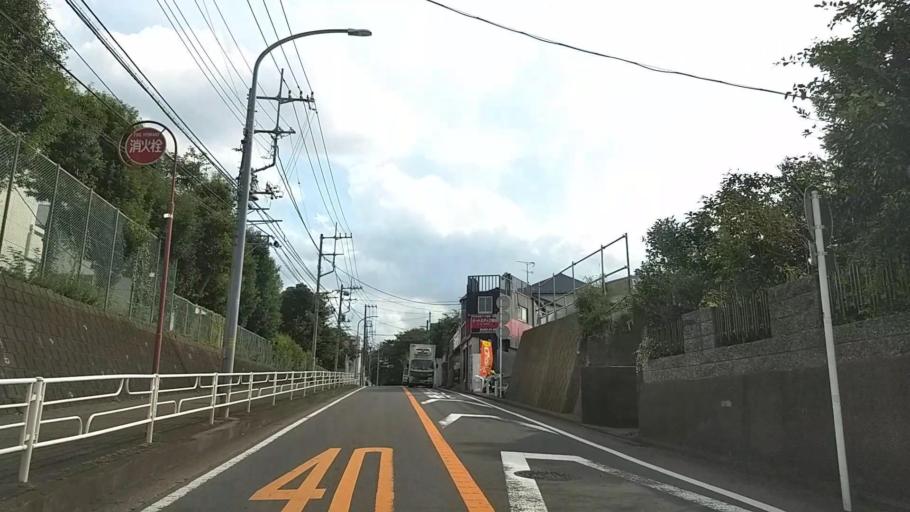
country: JP
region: Kanagawa
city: Yokohama
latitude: 35.4944
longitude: 139.5875
